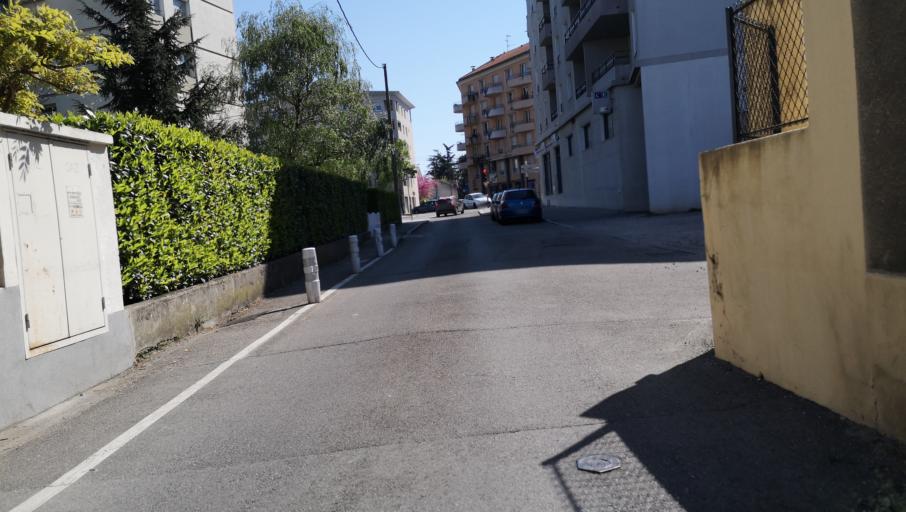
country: FR
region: Rhone-Alpes
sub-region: Departement du Rhone
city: Bron
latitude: 45.7328
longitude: 4.9128
